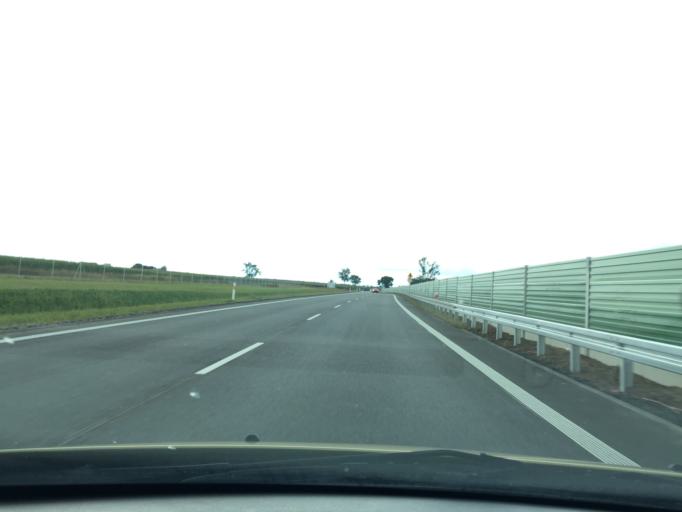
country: PL
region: Greater Poland Voivodeship
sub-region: Powiat sredzki
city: Nowe Miasto nad Warta
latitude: 52.0489
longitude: 17.4395
